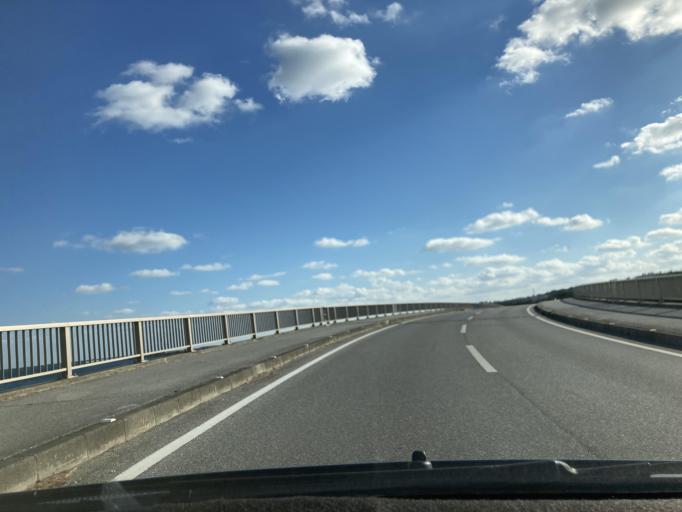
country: JP
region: Okinawa
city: Katsuren-haebaru
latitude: 26.3172
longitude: 127.9182
